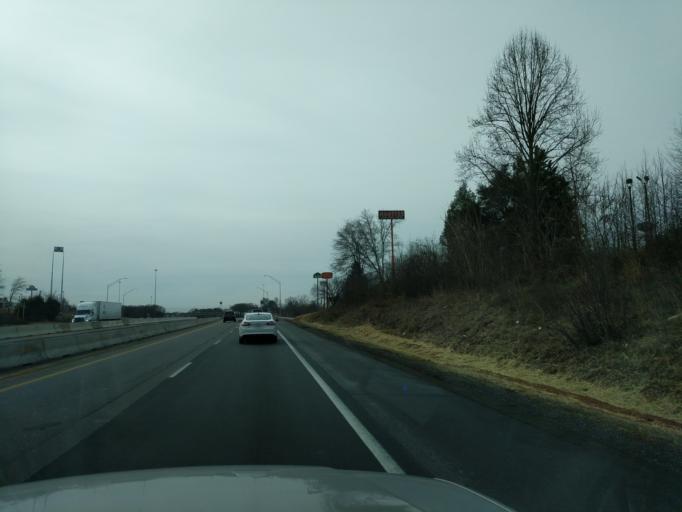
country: US
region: North Carolina
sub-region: Iredell County
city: Mooresville
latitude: 35.5985
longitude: -80.8603
